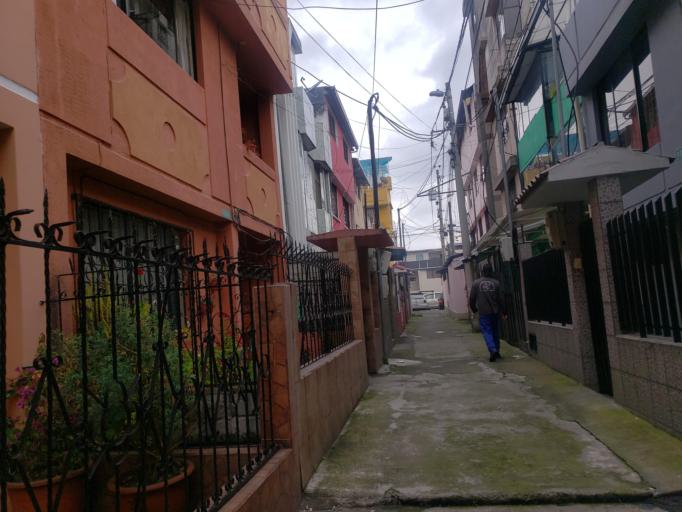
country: EC
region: Pichincha
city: Quito
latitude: -0.2674
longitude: -78.5441
